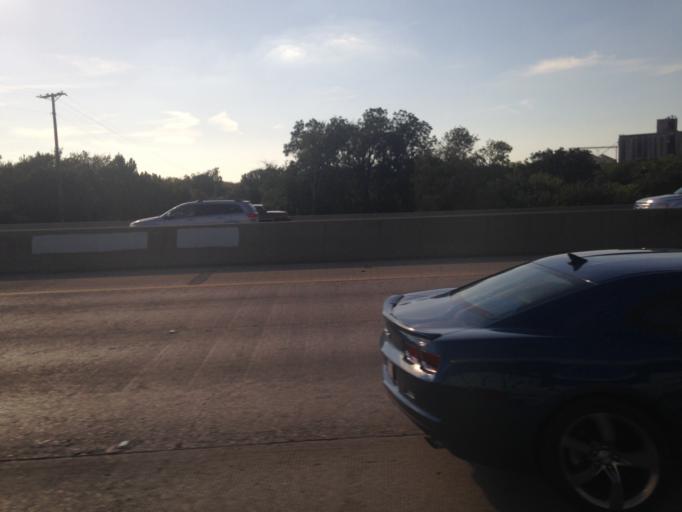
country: US
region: Texas
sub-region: Tarrant County
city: Fort Worth
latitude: 32.7170
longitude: -97.3204
